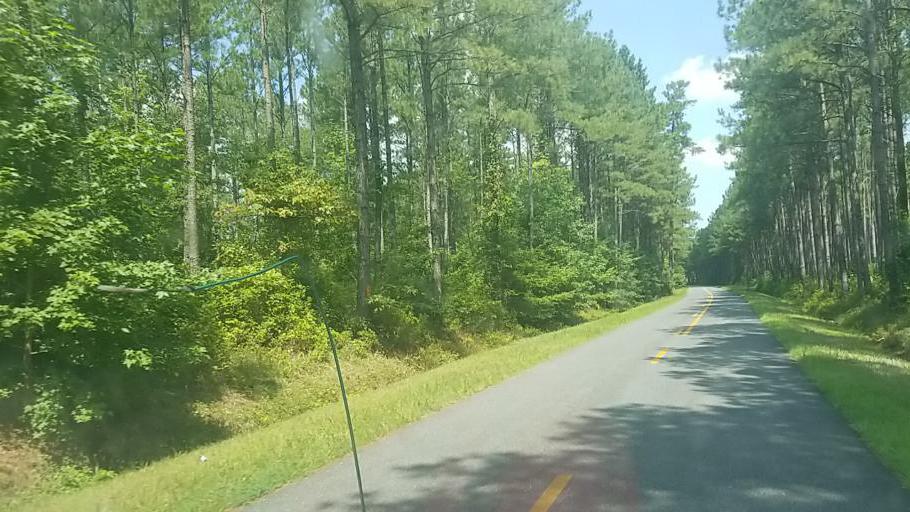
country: US
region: Maryland
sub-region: Worcester County
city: Snow Hill
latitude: 38.2714
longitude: -75.4716
